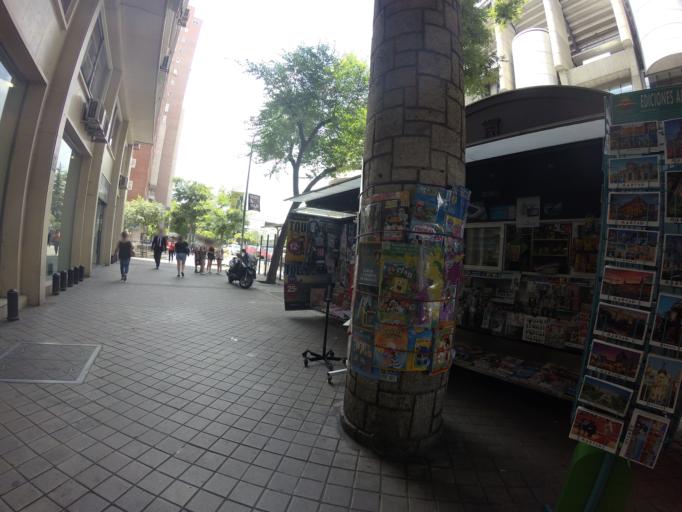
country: ES
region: Madrid
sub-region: Provincia de Madrid
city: Chamartin
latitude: 40.4519
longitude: -3.6886
